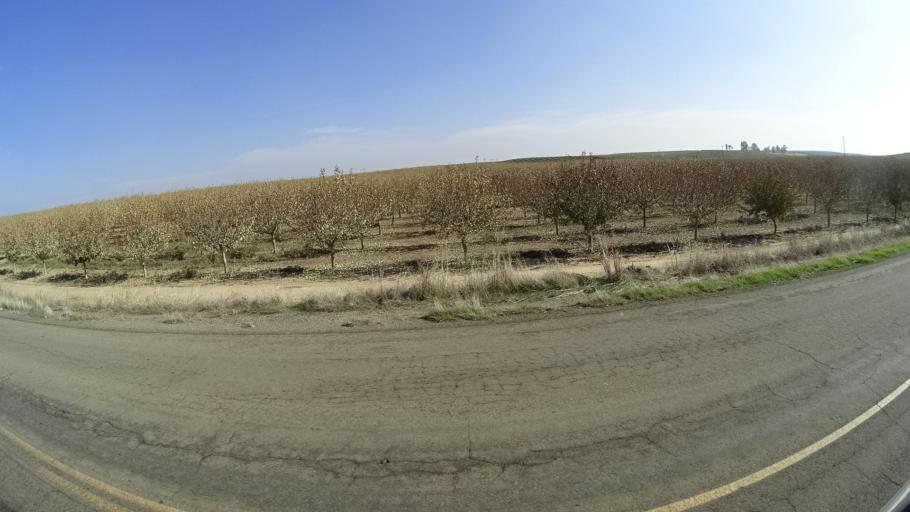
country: US
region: California
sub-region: Kern County
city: McFarland
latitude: 35.6436
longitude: -119.1336
